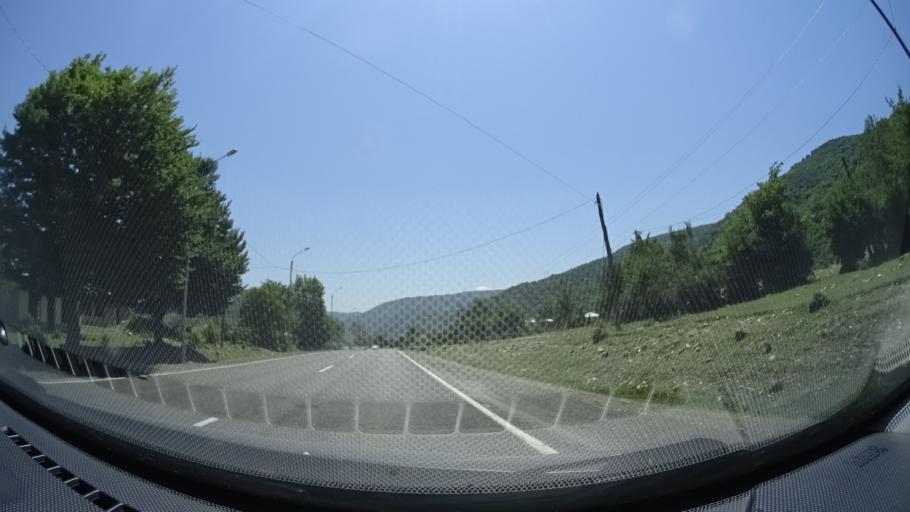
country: GE
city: Zhinvali
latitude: 42.2092
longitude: 44.6743
